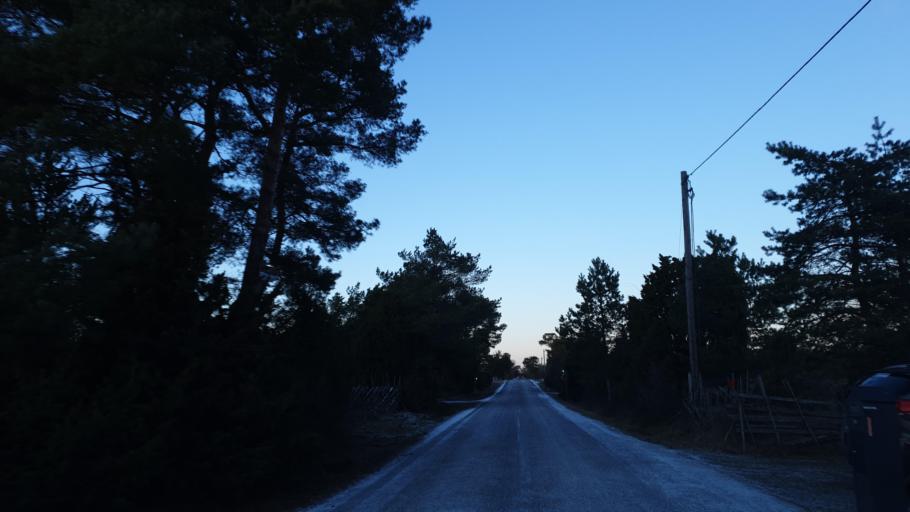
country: SE
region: Gotland
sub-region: Gotland
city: Slite
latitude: 57.3872
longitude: 18.8086
